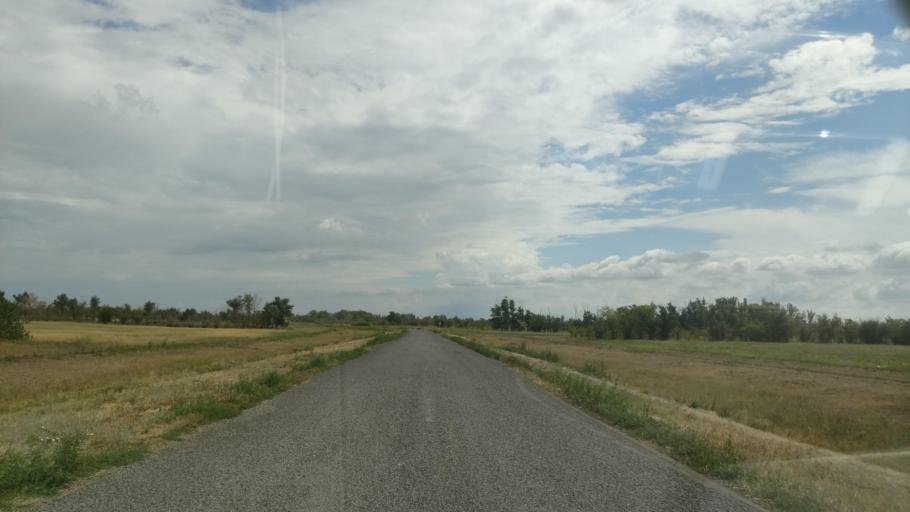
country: KZ
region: Pavlodar
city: Pavlodar
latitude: 52.6366
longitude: 76.9871
